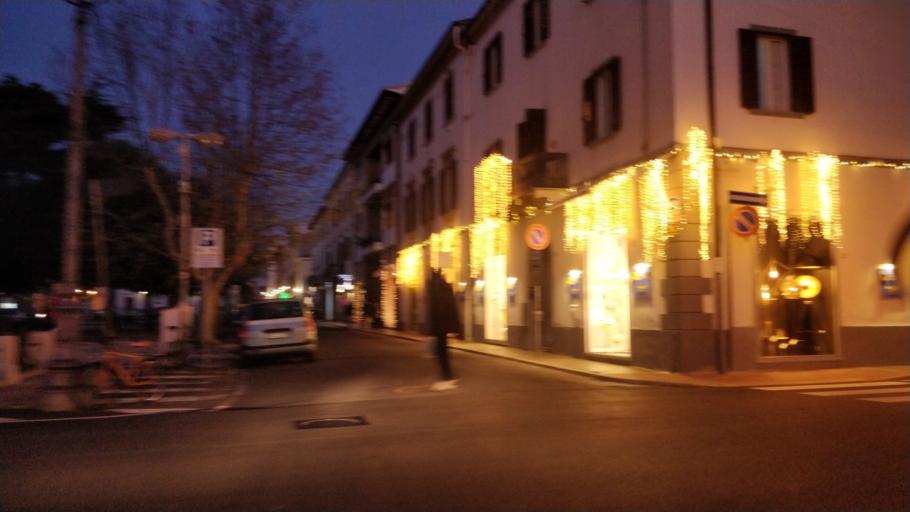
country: IT
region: Tuscany
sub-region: Provincia di Livorno
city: Cecina
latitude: 43.3105
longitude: 10.5149
